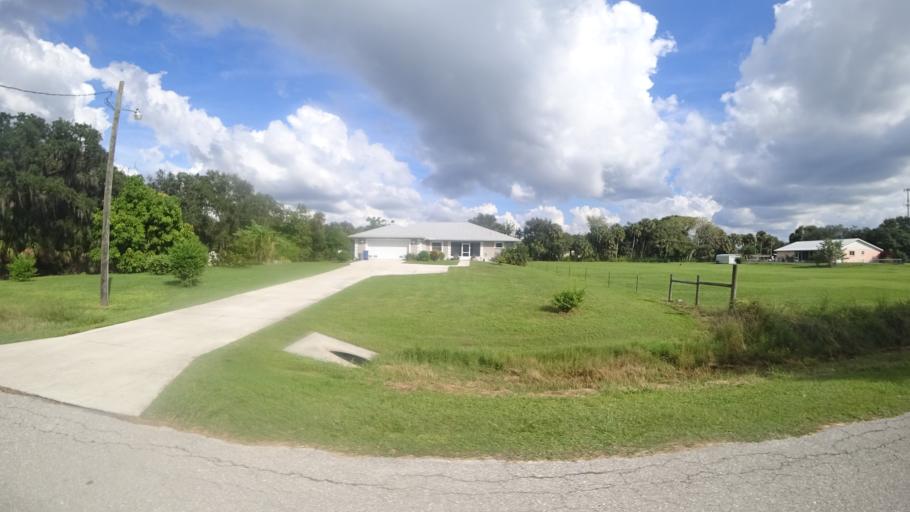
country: US
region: Florida
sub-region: Manatee County
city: Memphis
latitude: 27.5864
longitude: -82.5565
